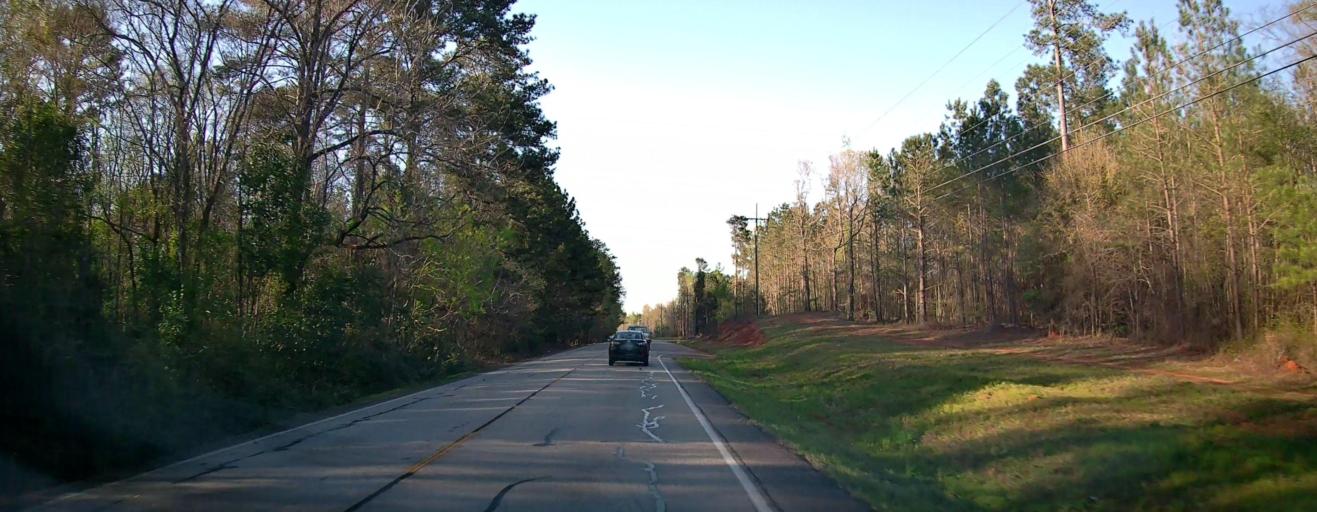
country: US
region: Georgia
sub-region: Newton County
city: Oakwood
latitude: 33.4246
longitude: -83.8952
